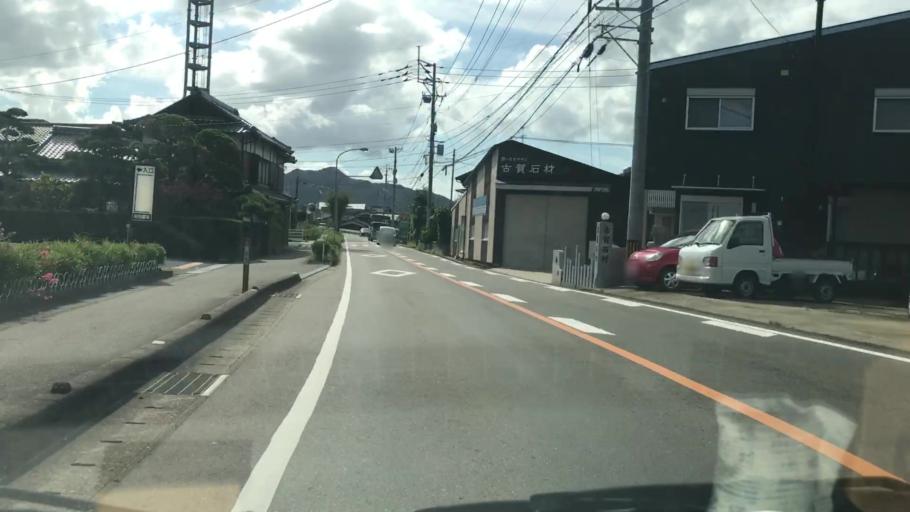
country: JP
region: Saga Prefecture
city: Kashima
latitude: 33.1260
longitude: 130.0661
